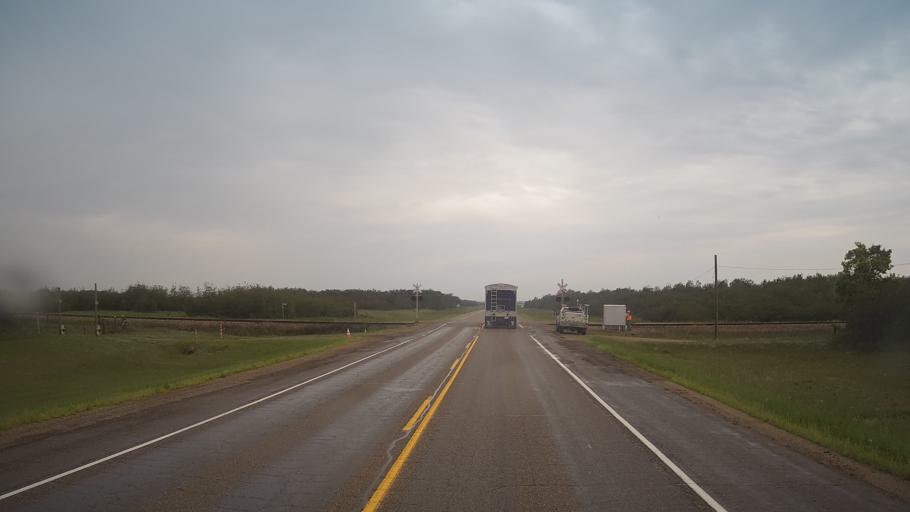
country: CA
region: Saskatchewan
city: Langham
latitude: 52.1294
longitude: -107.0494
